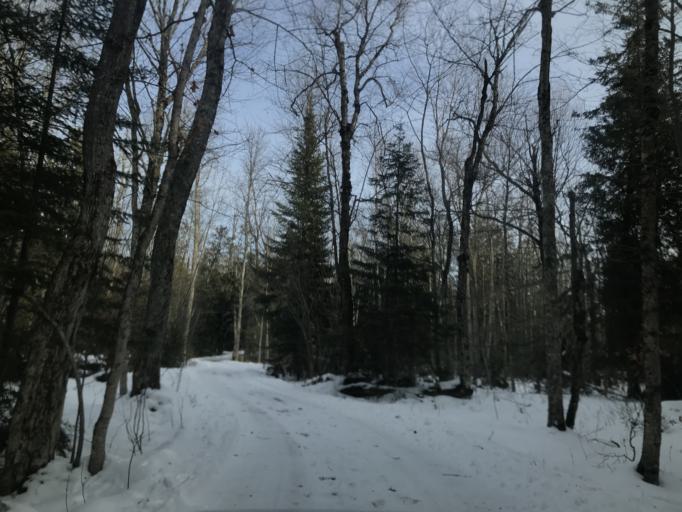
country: US
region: Wisconsin
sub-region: Door County
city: Sturgeon Bay
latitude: 45.1512
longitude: -87.0586
